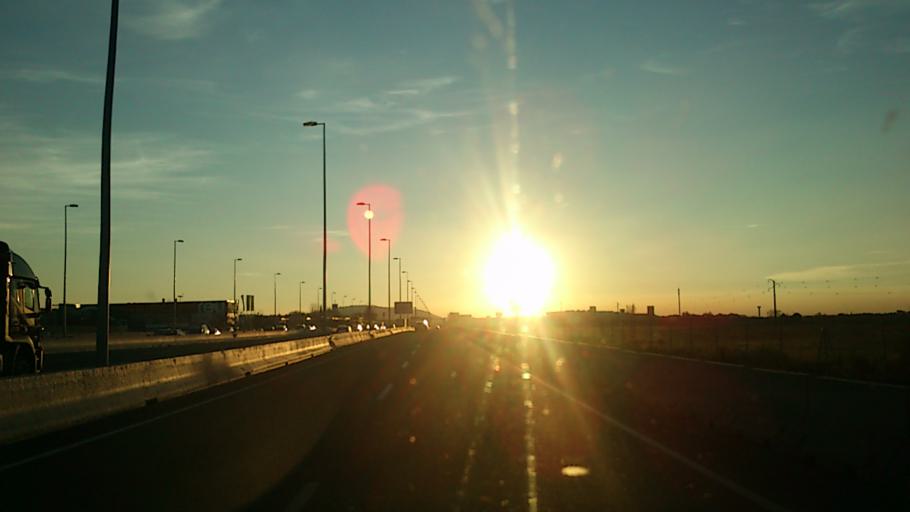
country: ES
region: Madrid
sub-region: Provincia de Madrid
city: Meco
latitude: 40.5116
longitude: -3.3207
